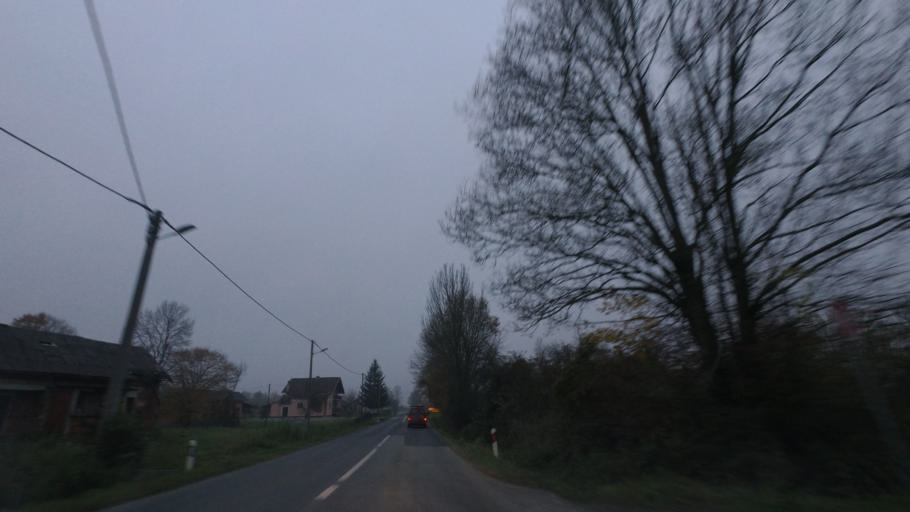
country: HR
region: Sisacko-Moslavacka
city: Petrinja
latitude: 45.4635
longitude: 16.2532
